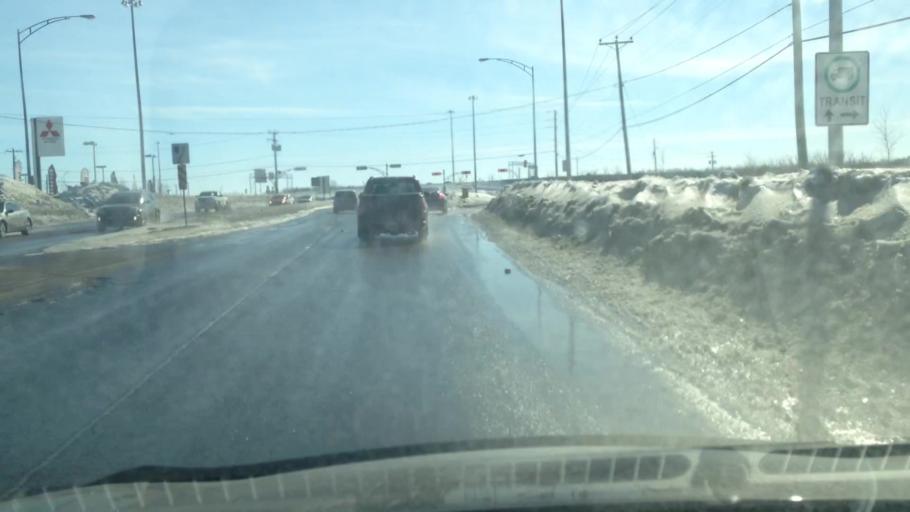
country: CA
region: Quebec
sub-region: Laurentides
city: Saint-Jerome
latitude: 45.7479
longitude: -74.0005
